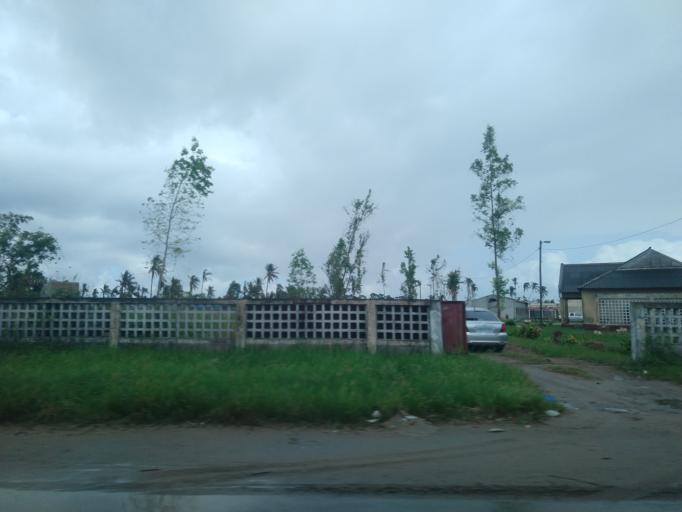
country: MZ
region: Sofala
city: Beira
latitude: -19.7863
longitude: 34.8821
